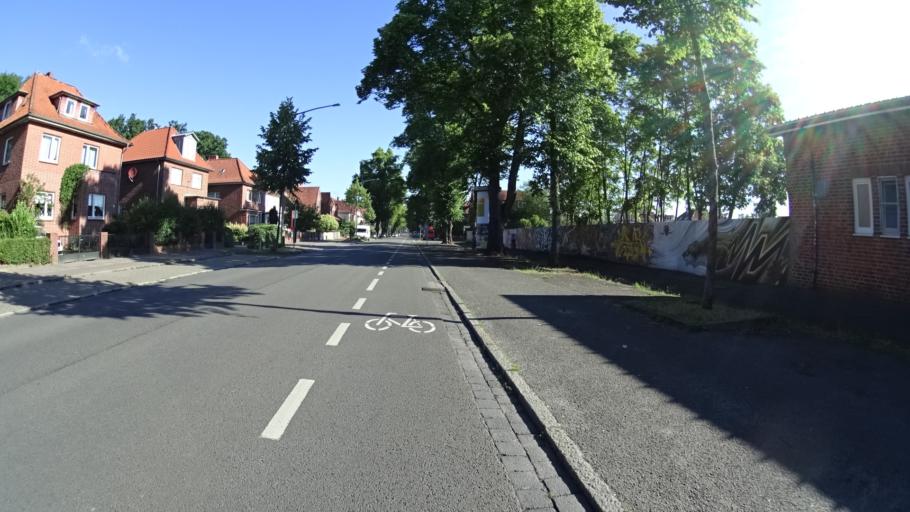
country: DE
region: Lower Saxony
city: Lueneburg
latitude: 53.2342
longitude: 10.4050
